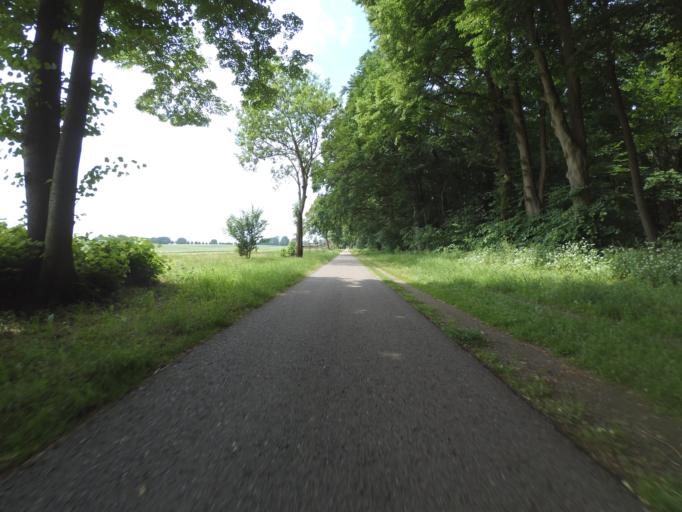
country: DE
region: Mecklenburg-Vorpommern
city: Malchow
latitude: 53.4904
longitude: 12.5003
